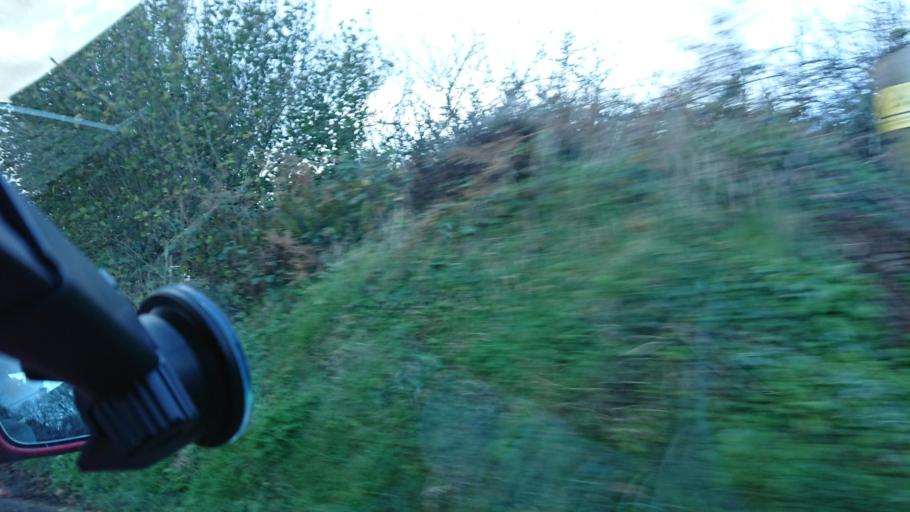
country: GB
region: England
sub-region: Cornwall
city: Looe
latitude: 50.3478
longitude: -4.4738
